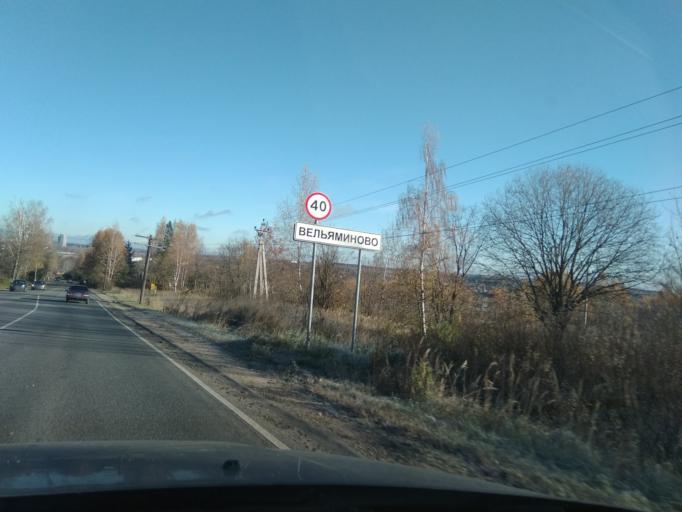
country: RU
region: Moskovskaya
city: Istra
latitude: 55.8830
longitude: 36.8587
